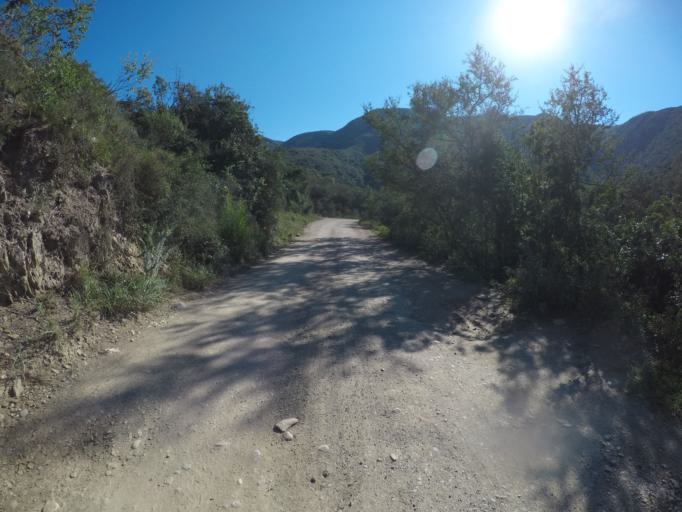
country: ZA
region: Eastern Cape
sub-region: Cacadu District Municipality
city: Kareedouw
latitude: -33.6583
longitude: 24.5260
